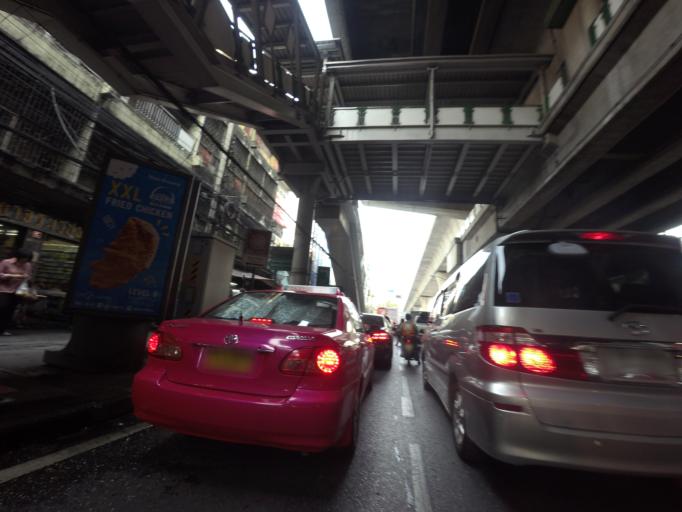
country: TH
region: Bangkok
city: Watthana
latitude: 13.7240
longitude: 100.5789
